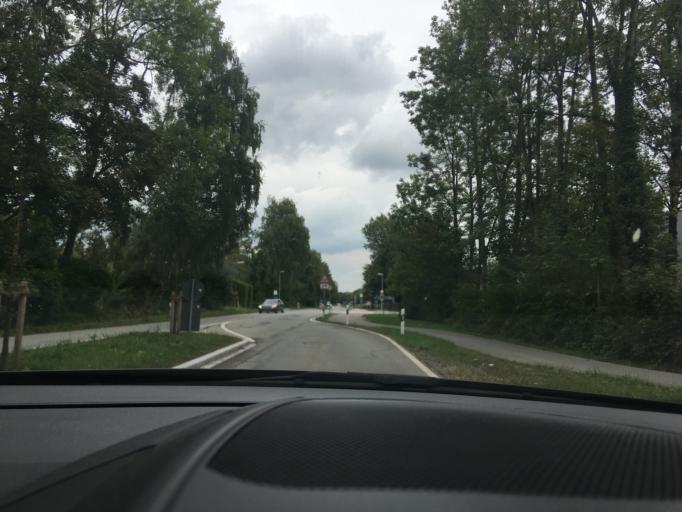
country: DE
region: Bavaria
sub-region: Upper Bavaria
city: Ismaning
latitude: 48.2382
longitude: 11.6792
